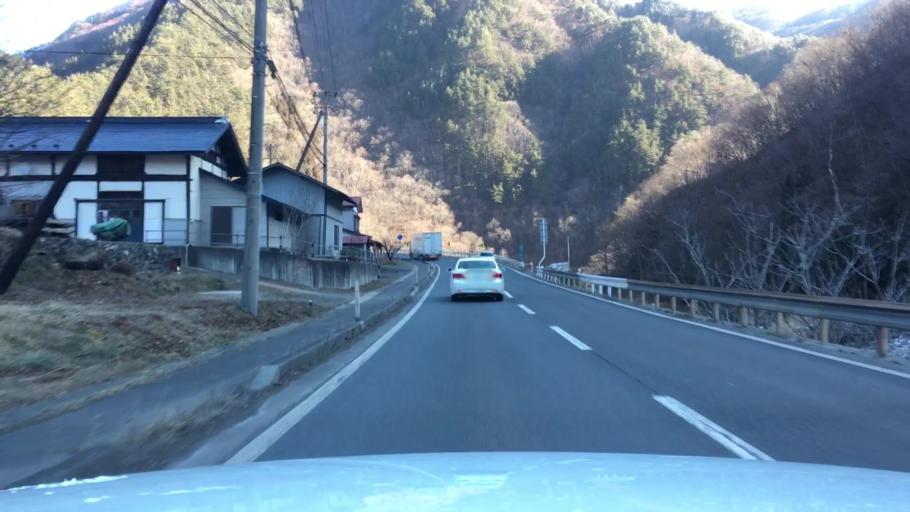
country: JP
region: Iwate
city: Miyako
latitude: 39.6101
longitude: 141.6434
